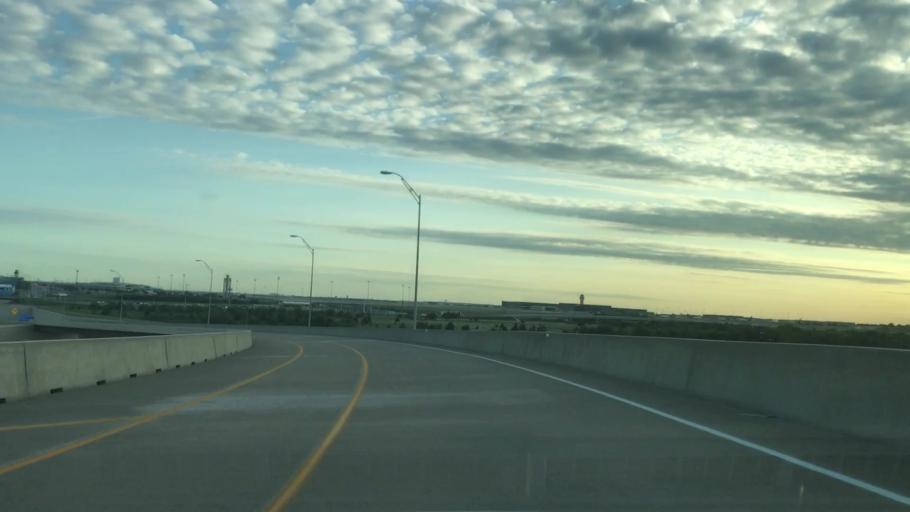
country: US
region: Texas
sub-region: Dallas County
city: Coppell
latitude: 32.9326
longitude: -97.0420
